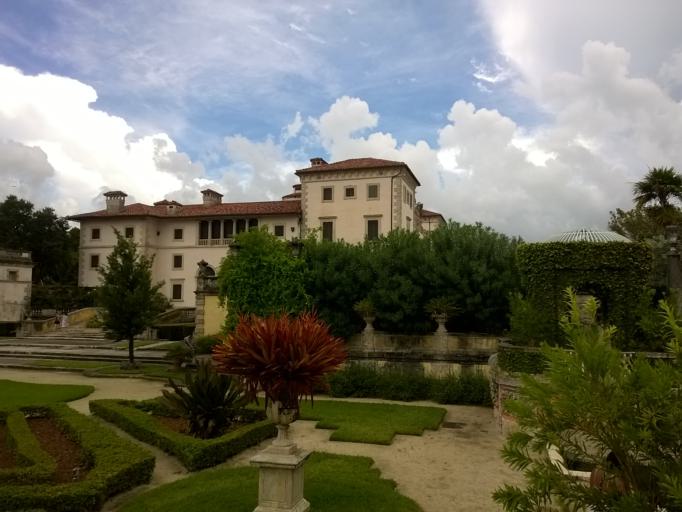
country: US
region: Florida
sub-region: Miami-Dade County
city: Miami
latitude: 25.7437
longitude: -80.2109
